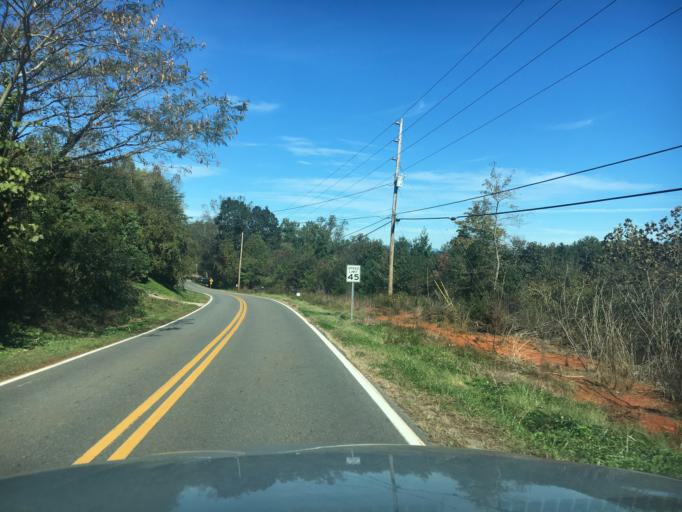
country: US
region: North Carolina
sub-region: Burke County
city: Salem
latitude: 35.7117
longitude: -81.7361
